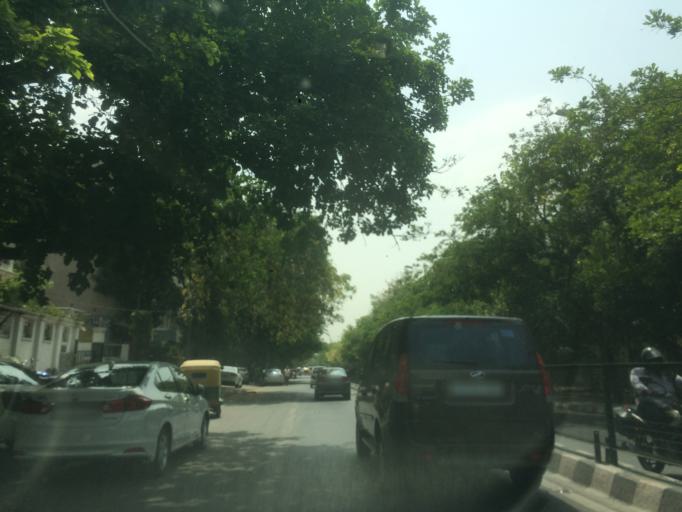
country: IN
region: NCT
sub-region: New Delhi
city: New Delhi
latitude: 28.5548
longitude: 77.2248
